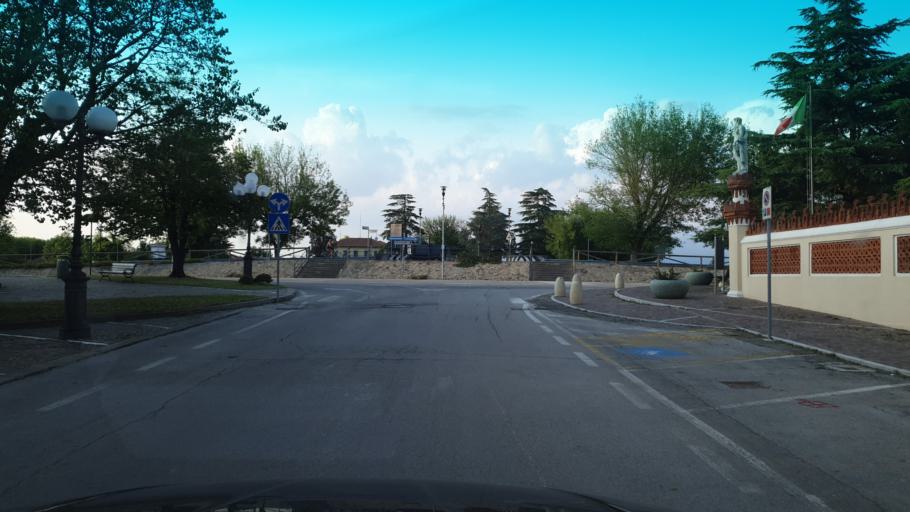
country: IT
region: Veneto
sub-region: Provincia di Rovigo
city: Castelguglielmo
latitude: 45.0251
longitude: 11.5377
